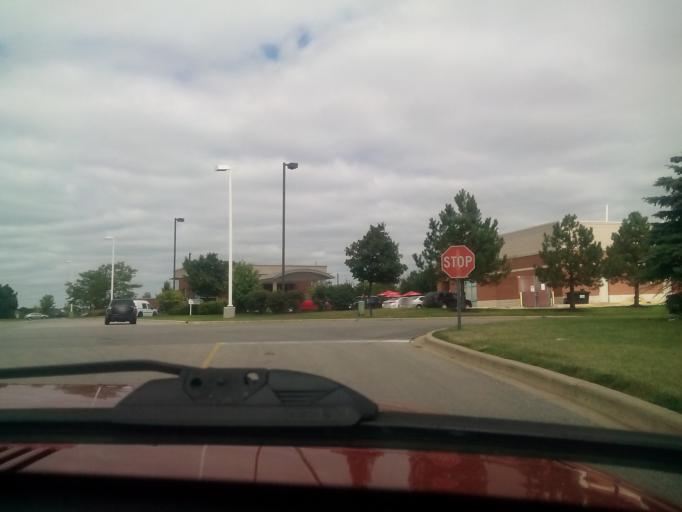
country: US
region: Illinois
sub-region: DuPage County
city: Woodridge
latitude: 41.7222
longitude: -88.0376
